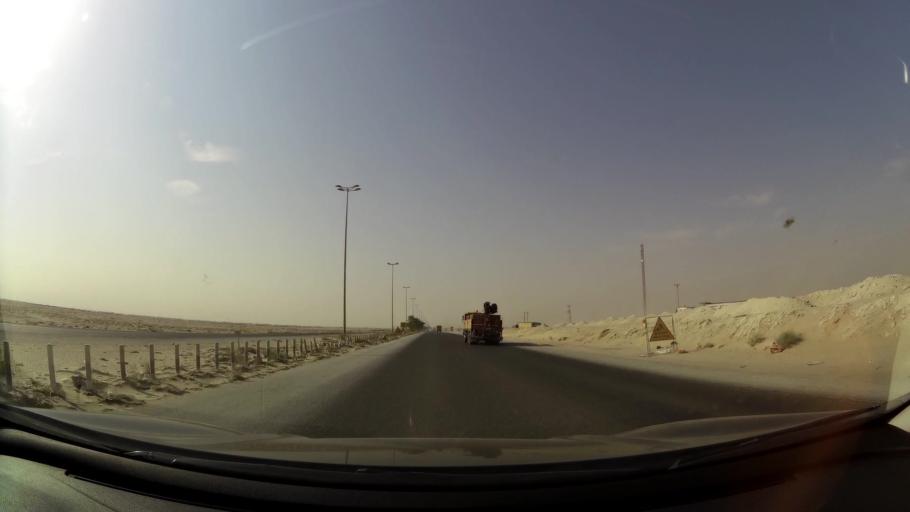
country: KW
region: Al Ahmadi
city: Al Ahmadi
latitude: 28.9045
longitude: 48.0929
